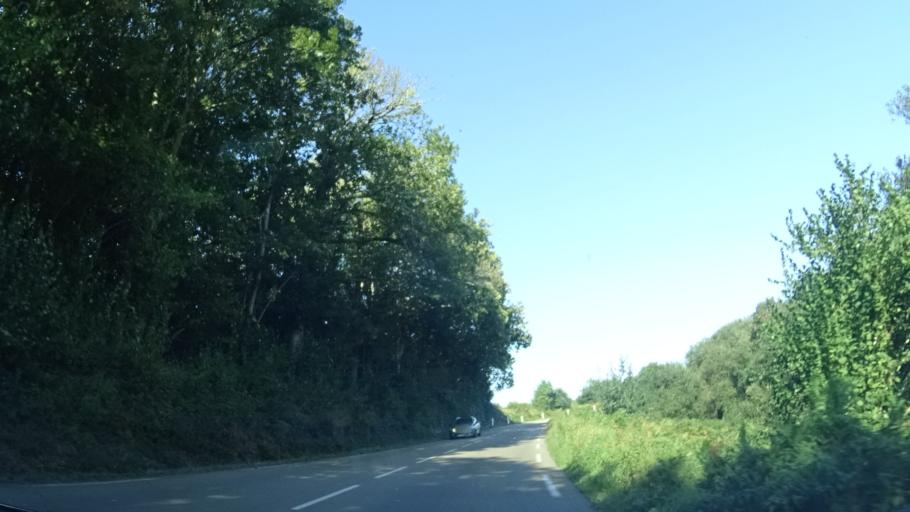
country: FR
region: Brittany
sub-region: Departement du Finistere
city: Douarnenez
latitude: 48.0934
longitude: -4.2882
